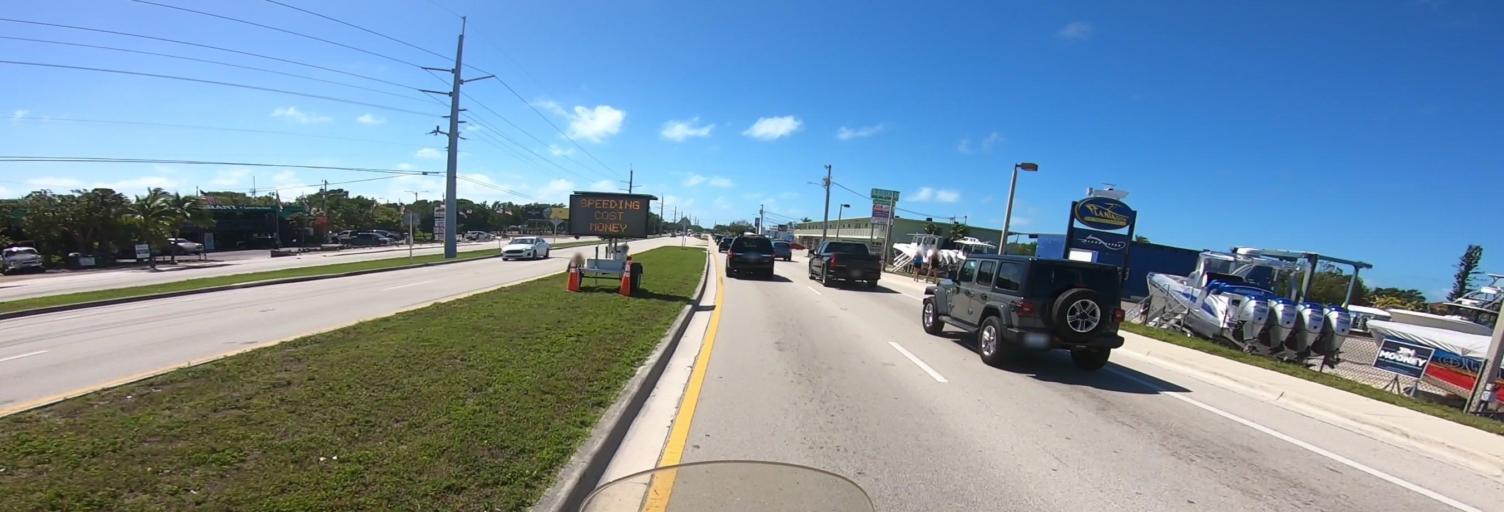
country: US
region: Florida
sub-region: Monroe County
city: Tavernier
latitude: 25.0001
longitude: -80.5371
